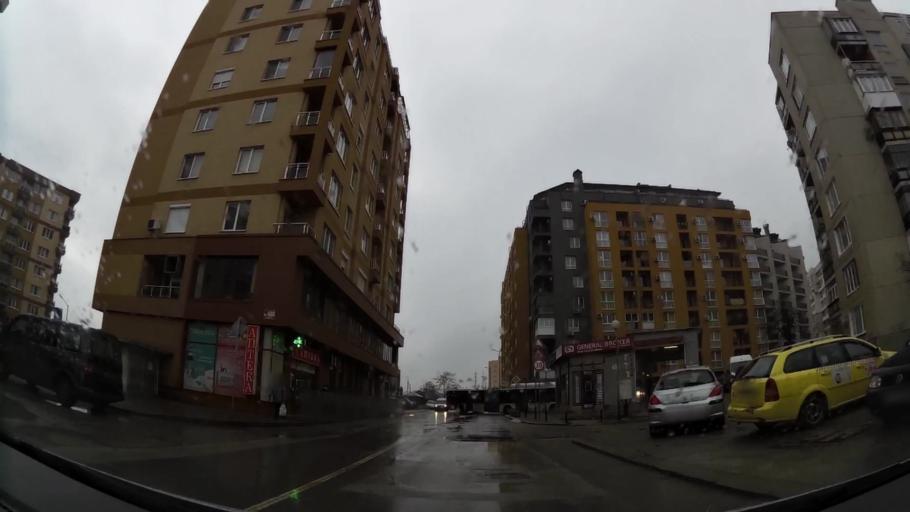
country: BG
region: Sofia-Capital
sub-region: Stolichna Obshtina
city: Sofia
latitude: 42.6270
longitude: 23.3840
